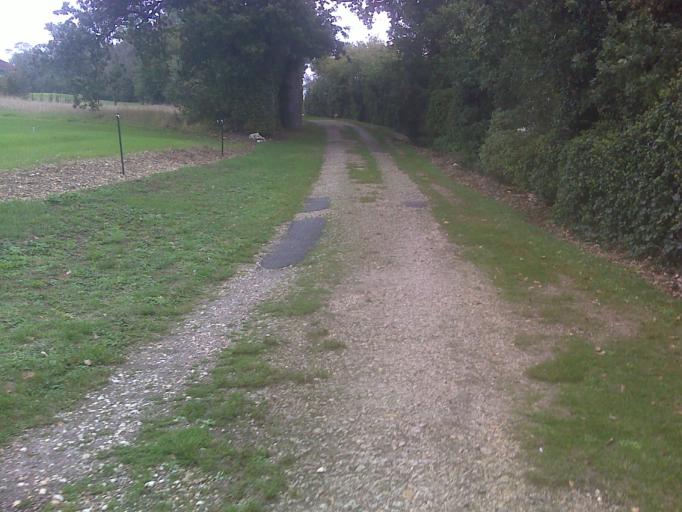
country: FR
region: Midi-Pyrenees
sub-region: Departement du Gers
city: Lectoure
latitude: 43.9440
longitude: 0.6437
